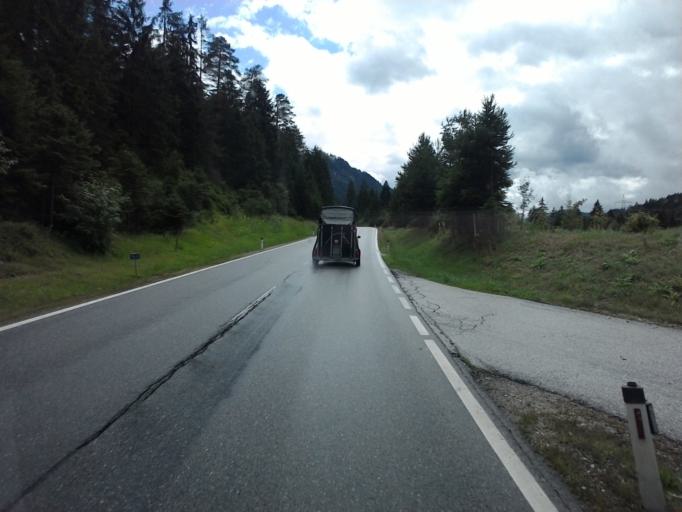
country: AT
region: Tyrol
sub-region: Politischer Bezirk Innsbruck Land
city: Scharnitz
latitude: 47.3610
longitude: 11.2288
